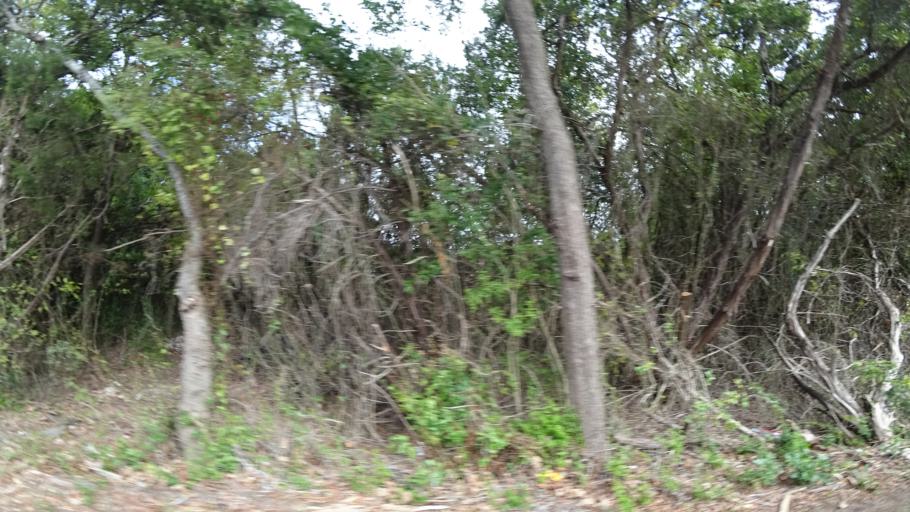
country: US
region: Texas
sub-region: Travis County
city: Shady Hollow
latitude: 30.2053
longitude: -97.8275
